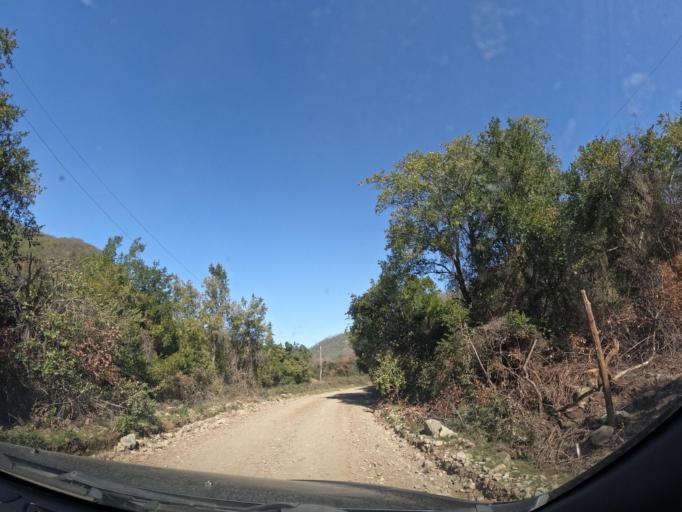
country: CL
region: Maule
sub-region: Provincia de Linares
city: Longavi
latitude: -36.2865
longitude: -71.4159
